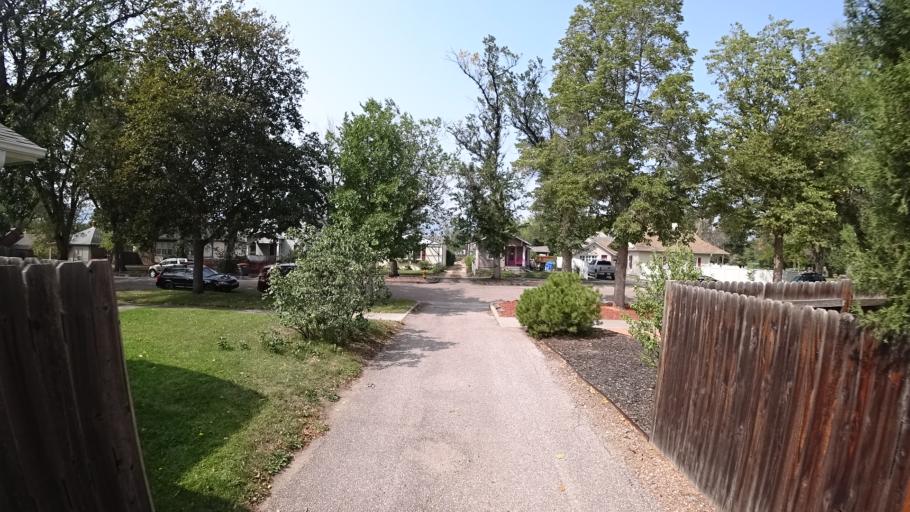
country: US
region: Colorado
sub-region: El Paso County
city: Colorado Springs
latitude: 38.8384
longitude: -104.8018
